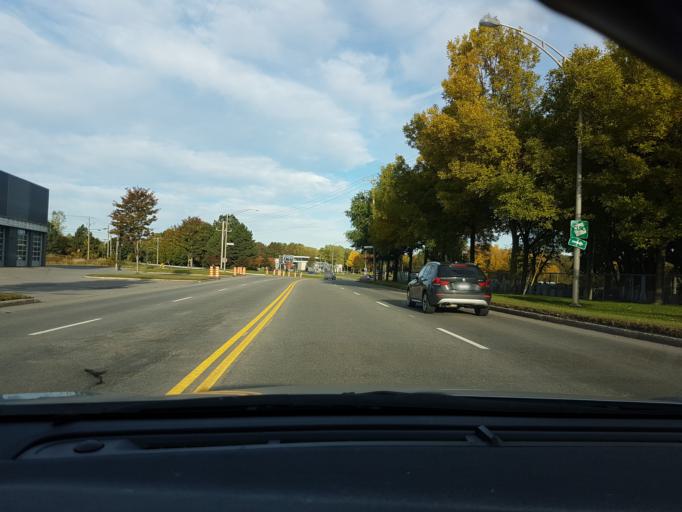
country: CA
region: Quebec
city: Quebec
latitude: 46.8066
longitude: -71.2674
